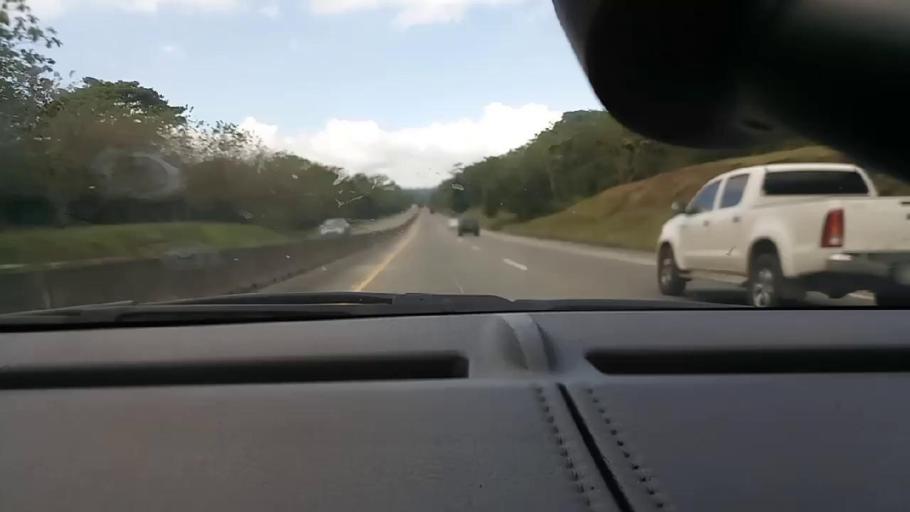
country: PA
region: Panama
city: Las Cumbres
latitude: 9.0720
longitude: -79.5773
